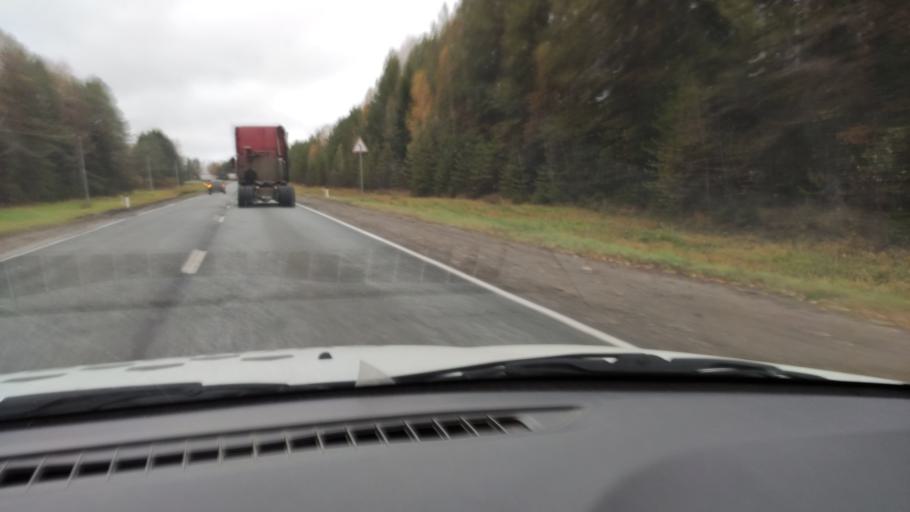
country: RU
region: Kirov
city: Belaya Kholunitsa
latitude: 58.8525
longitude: 50.7347
